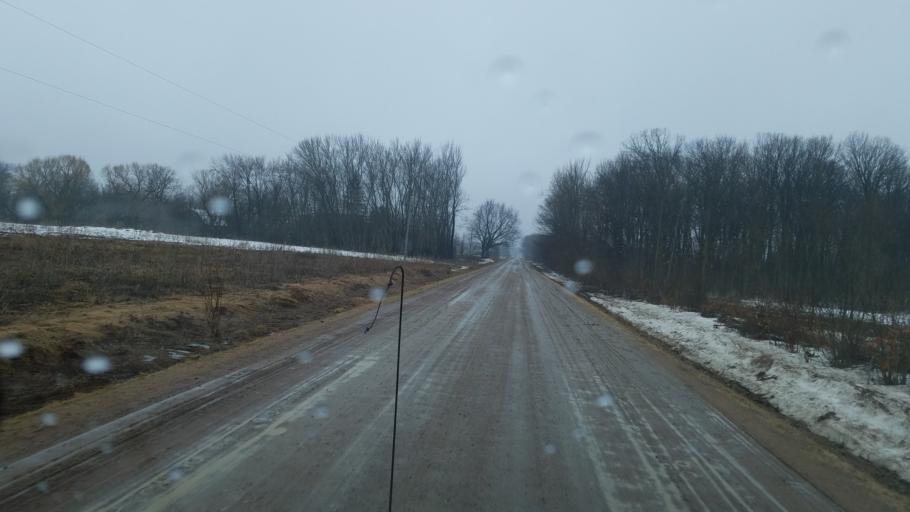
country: US
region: Wisconsin
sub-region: Clark County
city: Loyal
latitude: 44.6364
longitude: -90.3972
